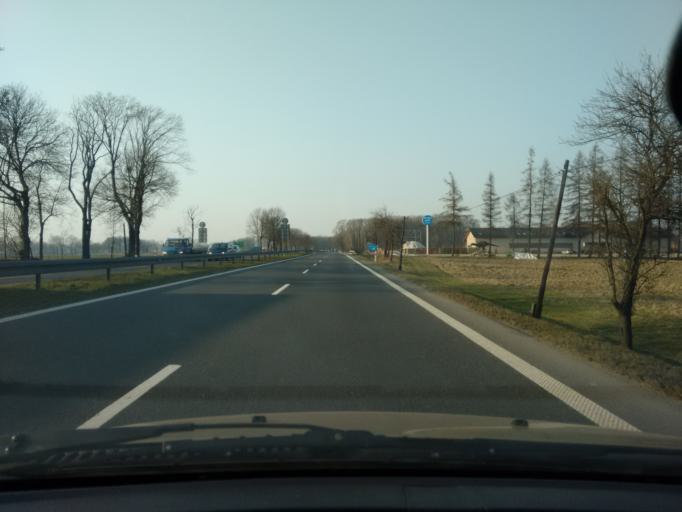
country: PL
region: Silesian Voivodeship
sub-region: Powiat cieszynski
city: Ochaby
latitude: 49.8535
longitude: 18.7602
